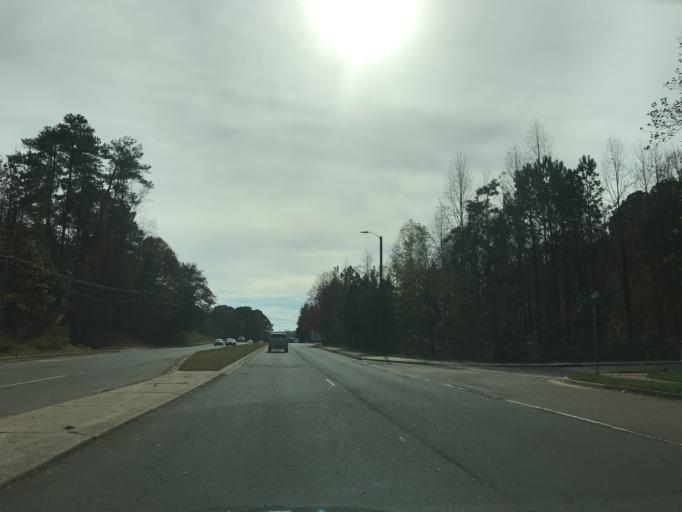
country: US
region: North Carolina
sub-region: Wake County
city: West Raleigh
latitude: 35.8476
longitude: -78.6803
